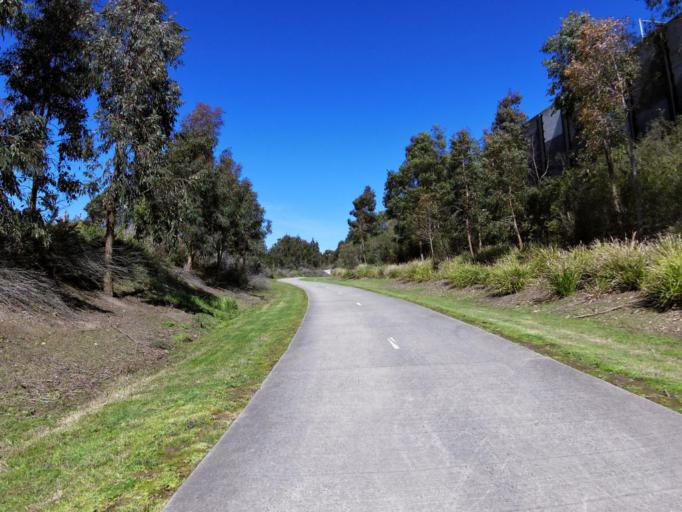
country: AU
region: Victoria
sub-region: Monash
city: Mulgrave
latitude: -37.9350
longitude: 145.2089
